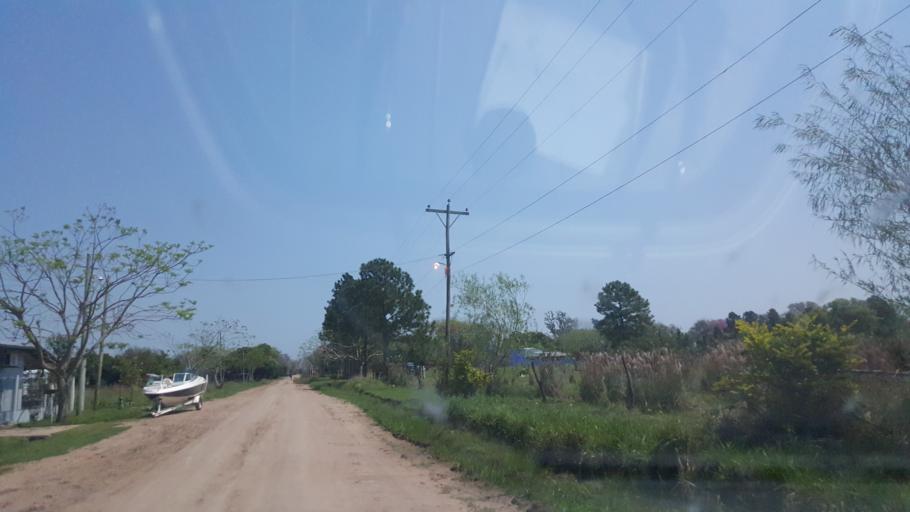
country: AR
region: Corrientes
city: Ita Ibate
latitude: -27.4242
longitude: -57.3262
